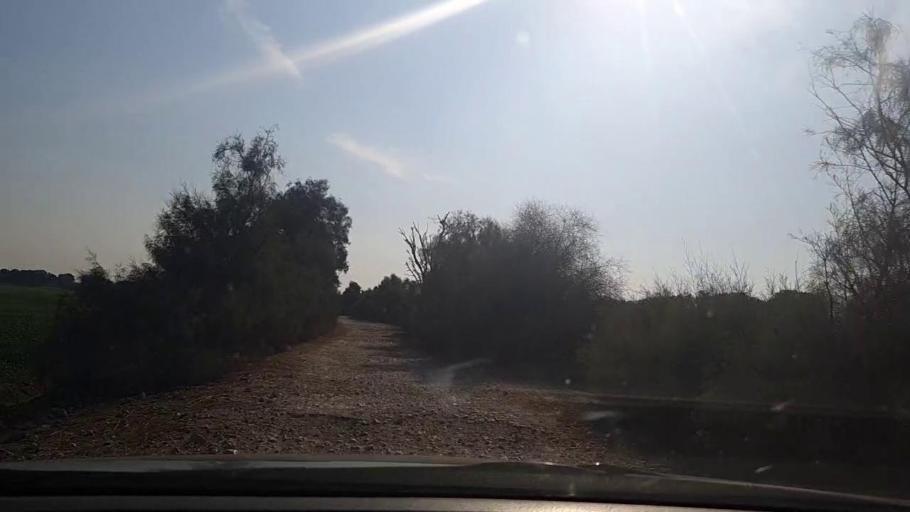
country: PK
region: Sindh
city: Sehwan
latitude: 26.3110
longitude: 68.0015
